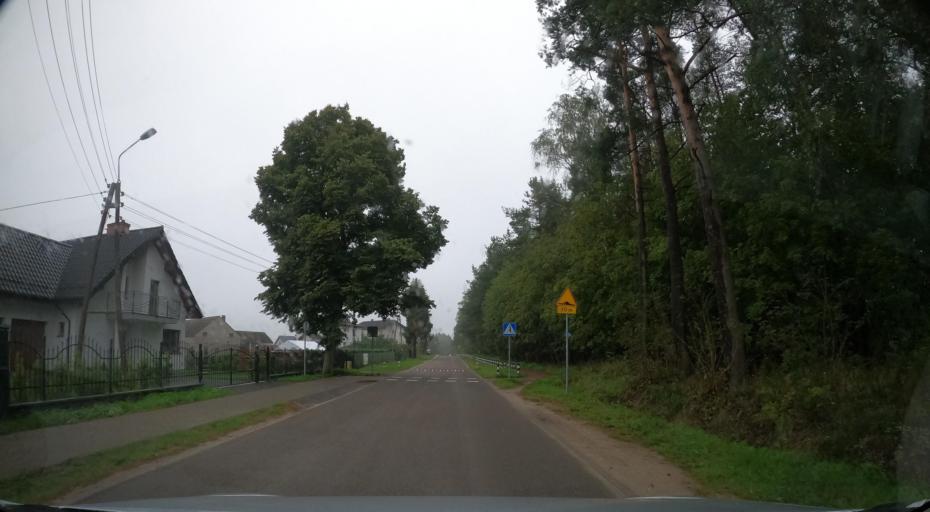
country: PL
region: Pomeranian Voivodeship
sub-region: Powiat kartuski
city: Chwaszczyno
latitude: 54.4381
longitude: 18.4182
